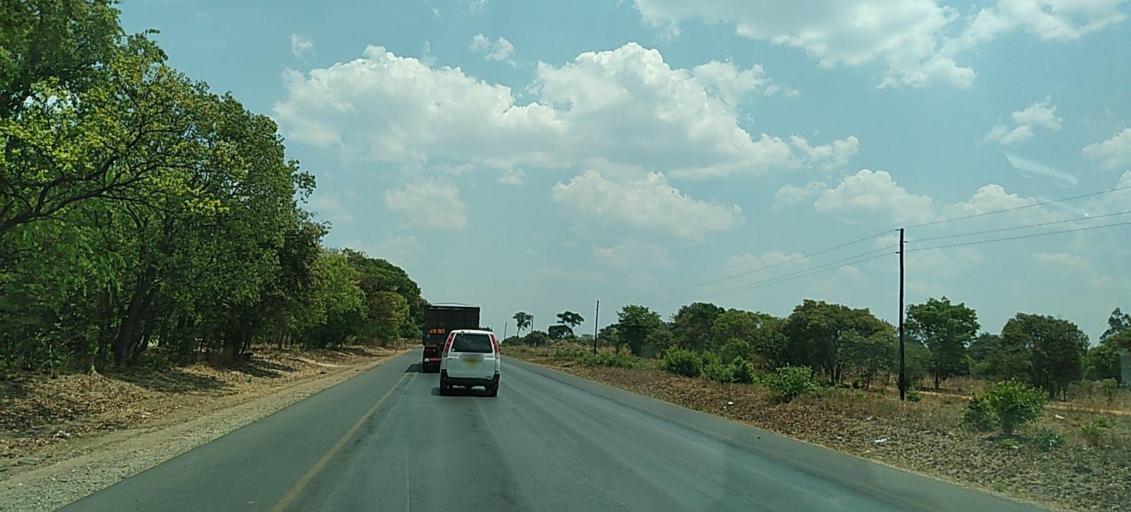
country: ZM
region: Central
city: Kabwe
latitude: -14.2285
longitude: 28.5732
